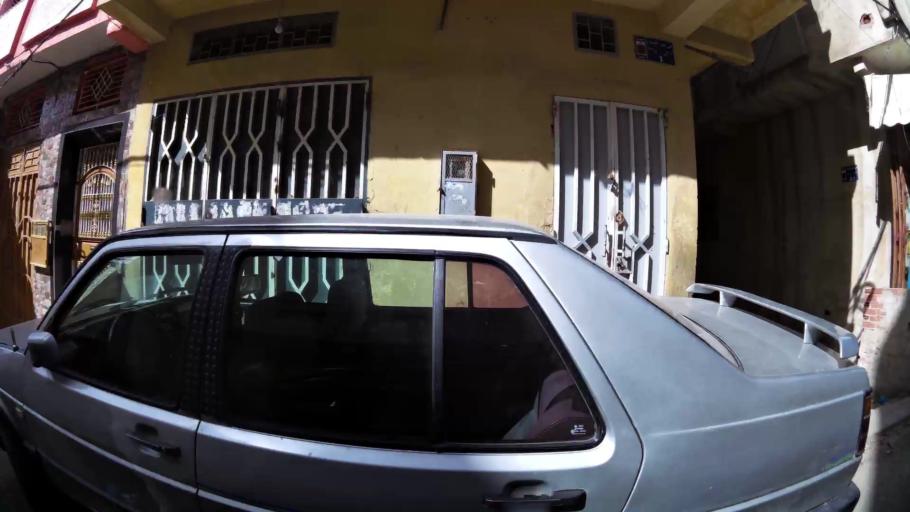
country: MA
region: Tanger-Tetouan
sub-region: Tanger-Assilah
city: Tangier
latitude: 35.7301
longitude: -5.8129
